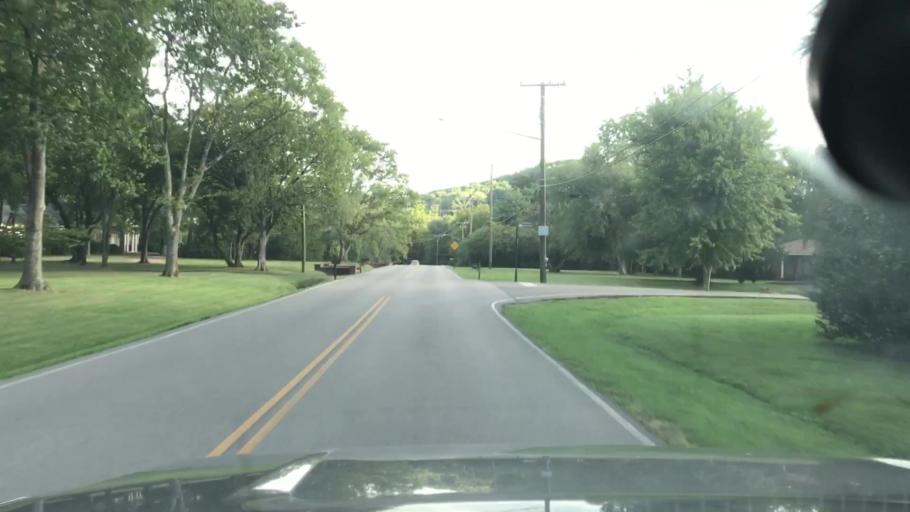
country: US
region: Tennessee
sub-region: Davidson County
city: Forest Hills
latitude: 36.0606
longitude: -86.8459
